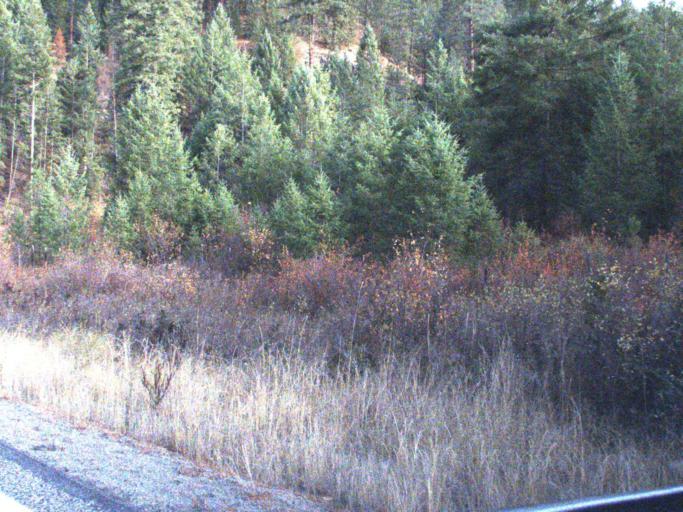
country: US
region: Washington
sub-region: Stevens County
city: Kettle Falls
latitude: 48.8141
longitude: -117.9311
